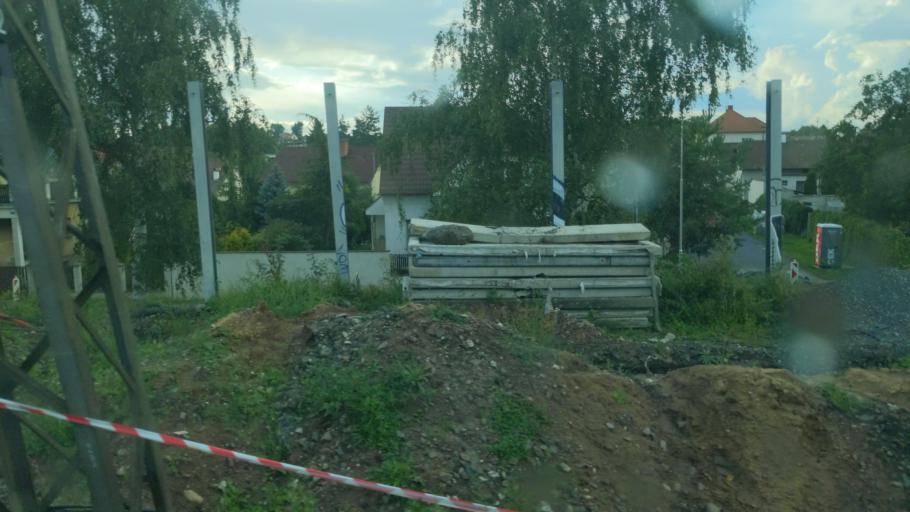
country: CZ
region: Central Bohemia
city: Poricany
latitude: 50.1082
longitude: 14.9164
